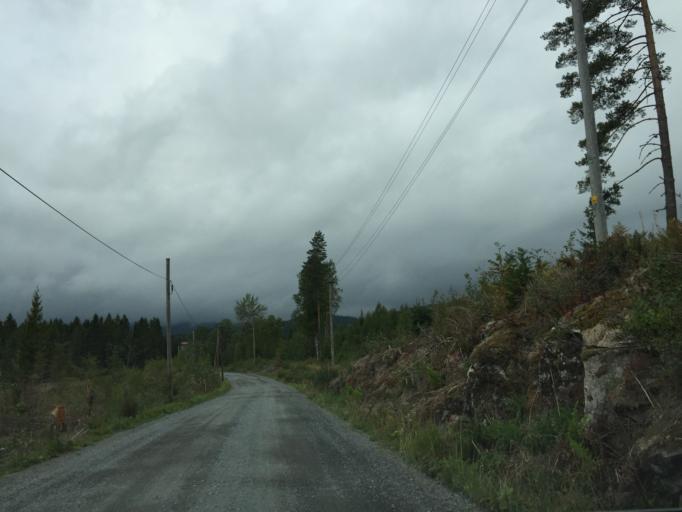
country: NO
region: Akershus
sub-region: Baerum
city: Lysaker
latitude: 60.0192
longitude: 10.5702
